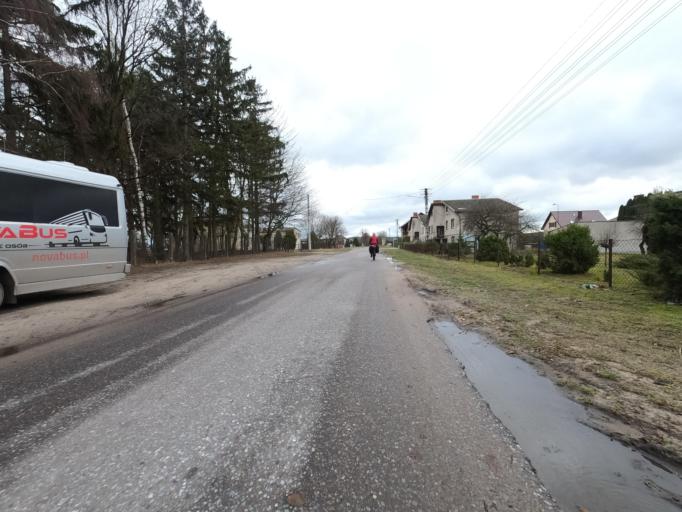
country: PL
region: Greater Poland Voivodeship
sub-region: Powiat pilski
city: Miasteczko Krajenskie
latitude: 53.1103
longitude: 17.0114
